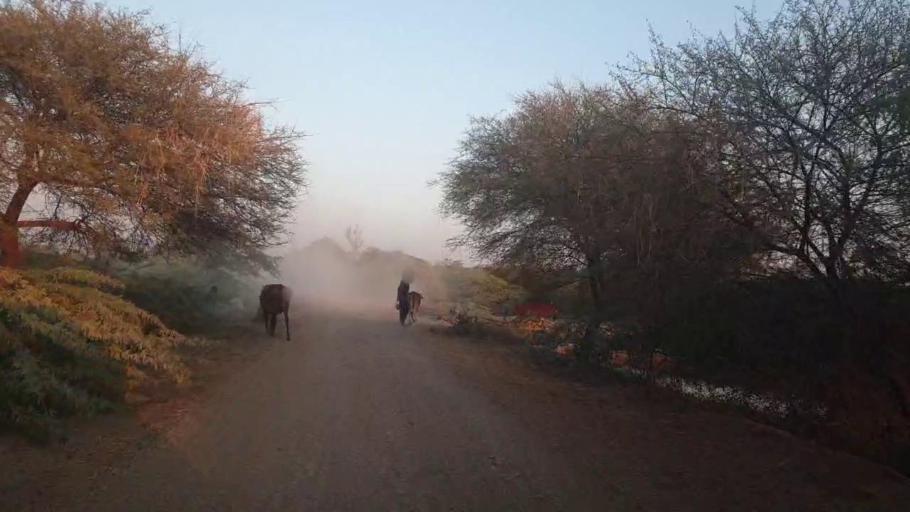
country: PK
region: Sindh
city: Mirpur Sakro
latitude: 24.4201
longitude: 67.5747
